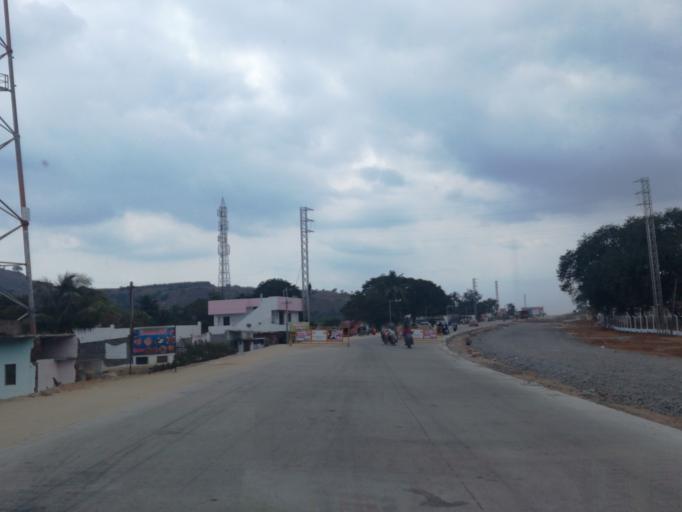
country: IN
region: Andhra Pradesh
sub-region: Chittoor
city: Ramapuram
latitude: 13.0939
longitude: 79.1331
